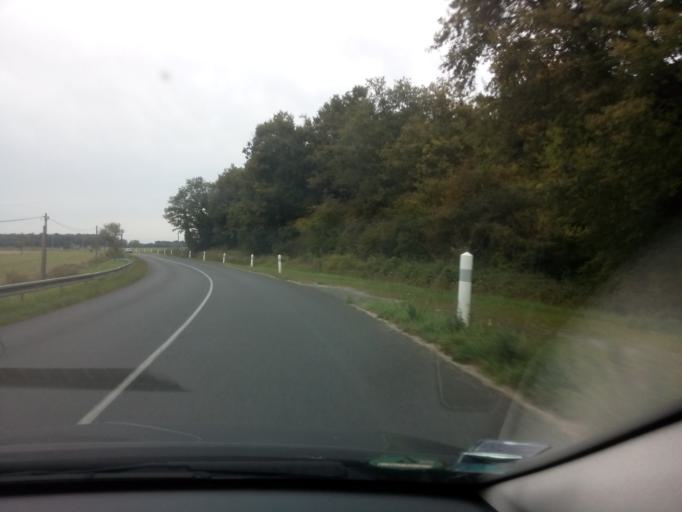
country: FR
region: Pays de la Loire
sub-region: Departement de Maine-et-Loire
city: Seiches-sur-le-Loir
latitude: 47.5578
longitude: -0.3337
